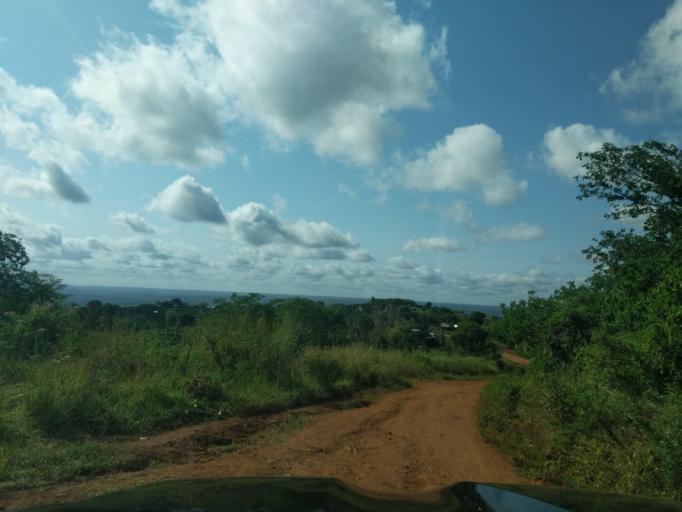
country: TZ
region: Tanga
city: Muheza
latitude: -5.4204
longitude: 38.6307
